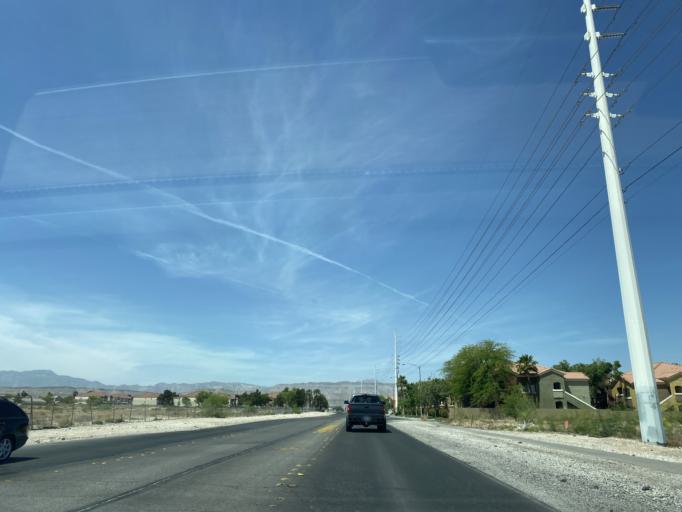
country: US
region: Nevada
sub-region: Clark County
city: Spring Valley
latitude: 36.0852
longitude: -115.2486
